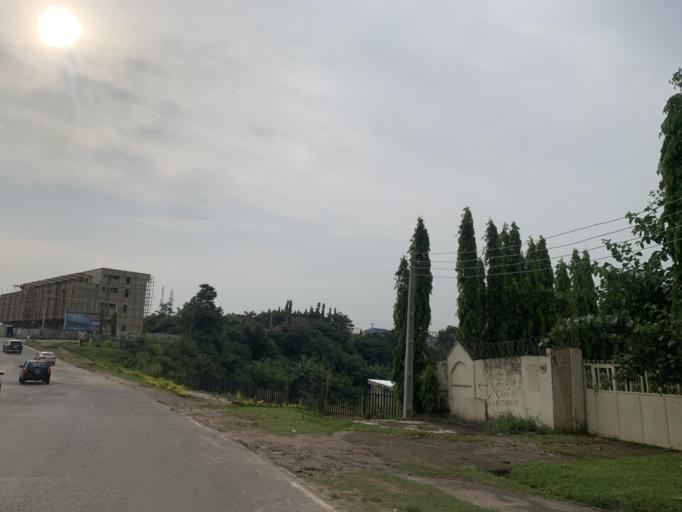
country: NG
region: Abuja Federal Capital Territory
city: Abuja
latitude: 9.1172
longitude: 7.4026
